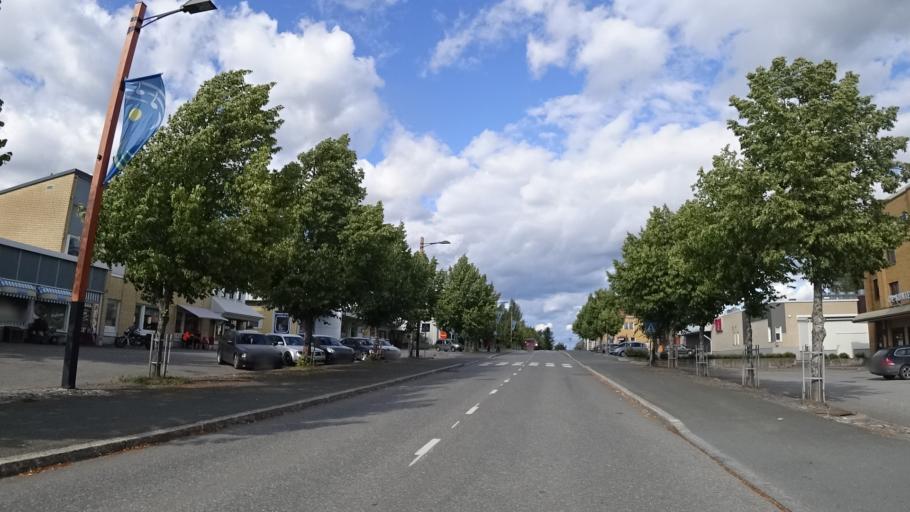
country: FI
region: North Karelia
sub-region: Keski-Karjala
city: Tohmajaervi
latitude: 62.2243
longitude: 30.3297
